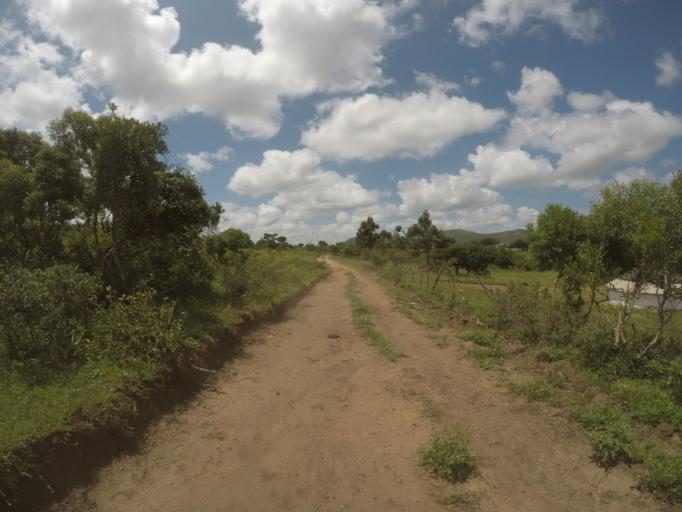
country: ZA
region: KwaZulu-Natal
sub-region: uThungulu District Municipality
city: Empangeni
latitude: -28.5816
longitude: 31.8413
